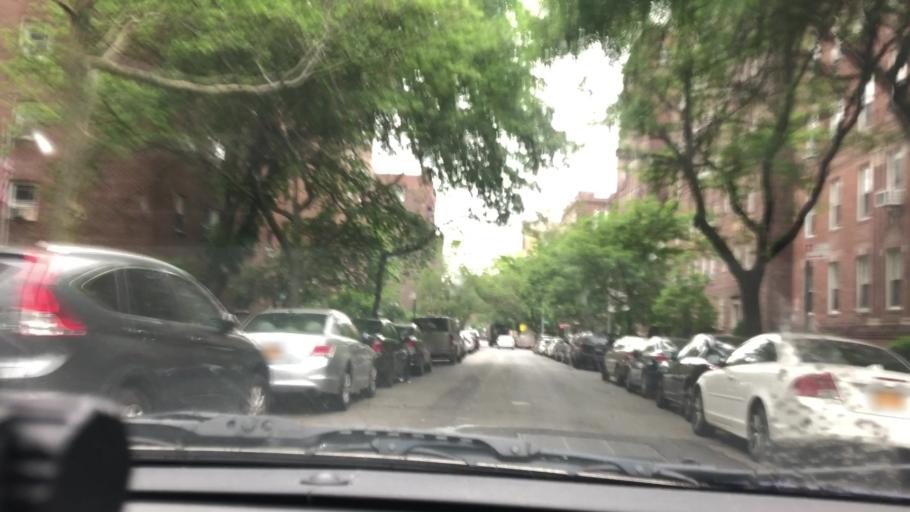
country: US
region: New York
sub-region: Queens County
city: Borough of Queens
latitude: 40.7173
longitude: -73.8386
